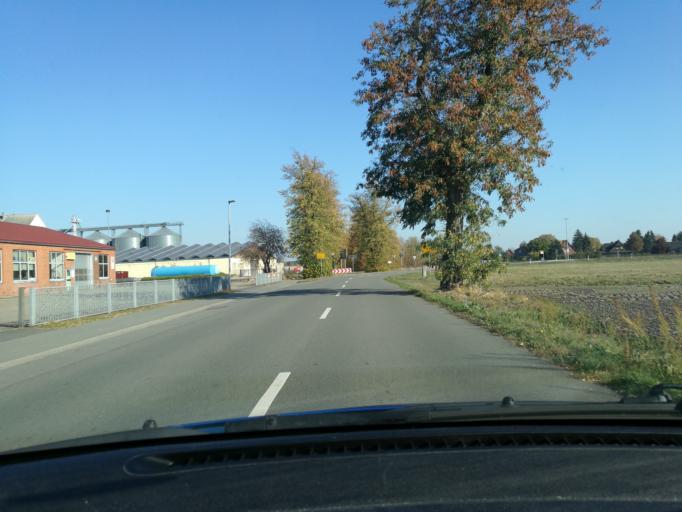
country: DE
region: Lower Saxony
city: Dannenberg
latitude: 53.1032
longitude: 11.1210
